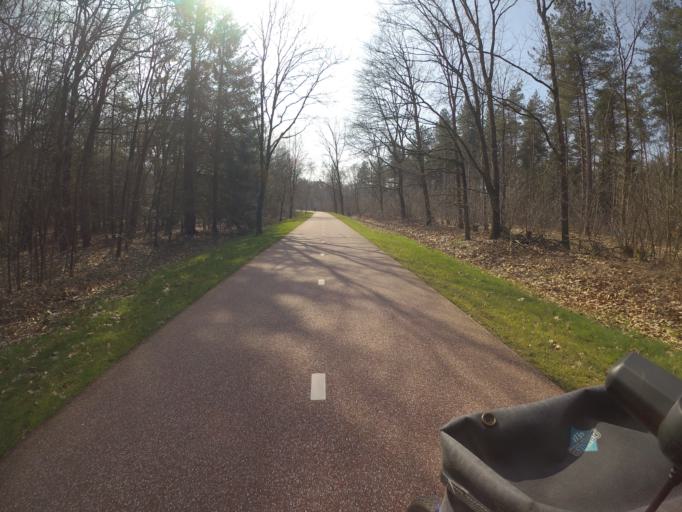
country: NL
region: North Brabant
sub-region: Gemeente Goirle
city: Goirle
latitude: 51.5557
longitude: 5.0211
